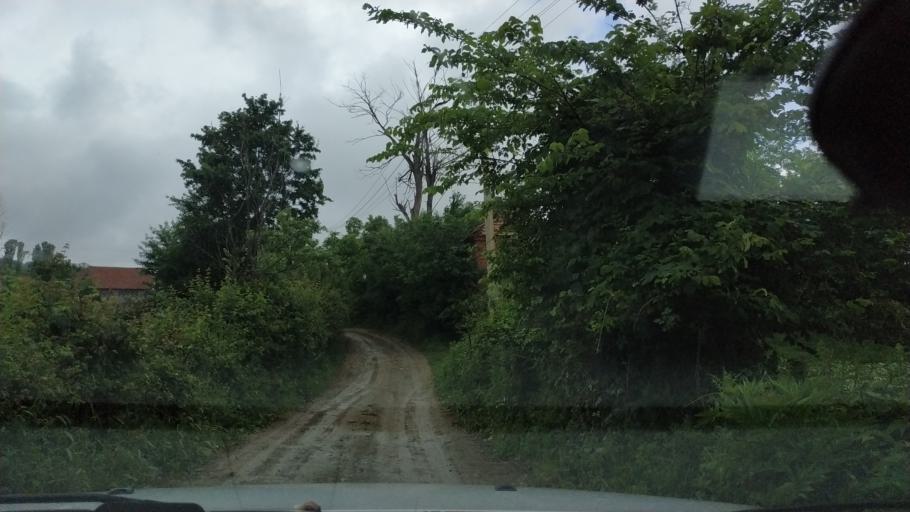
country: RS
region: Central Serbia
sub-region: Toplicki Okrug
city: Prokuplje
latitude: 43.3997
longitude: 21.5583
